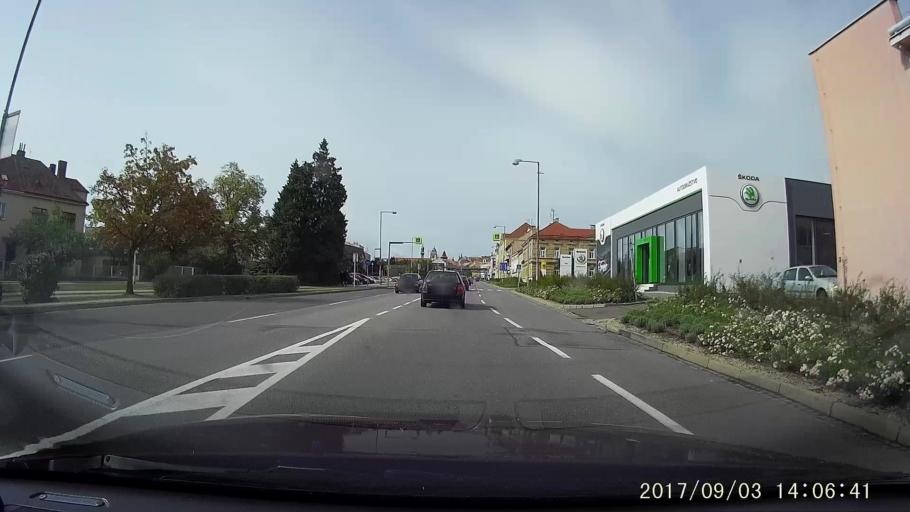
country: CZ
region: South Moravian
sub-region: Okres Znojmo
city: Znojmo
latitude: 48.8474
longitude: 16.0569
